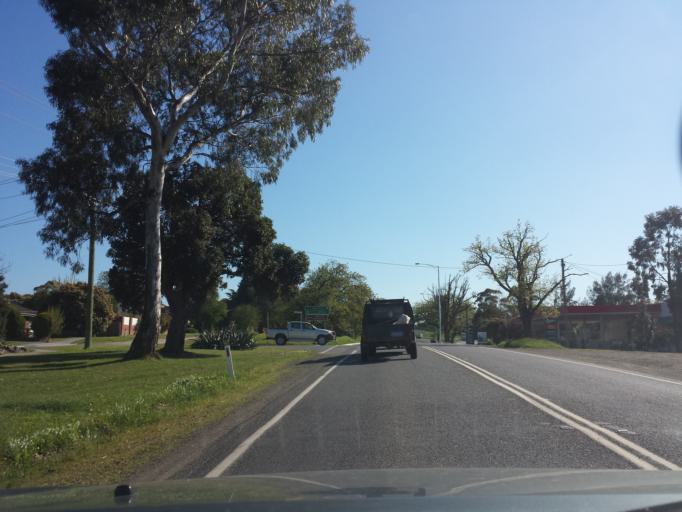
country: AU
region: Victoria
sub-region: Yarra Ranges
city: Yarra Glen
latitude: -37.6547
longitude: 145.3753
